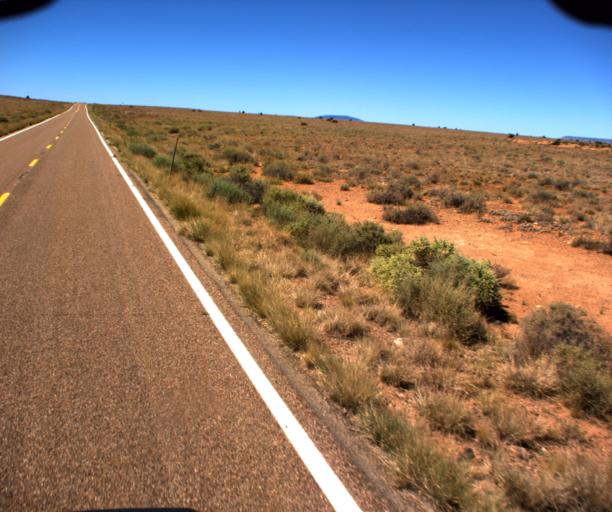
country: US
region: Arizona
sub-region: Navajo County
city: Winslow
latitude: 34.9080
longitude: -110.6399
